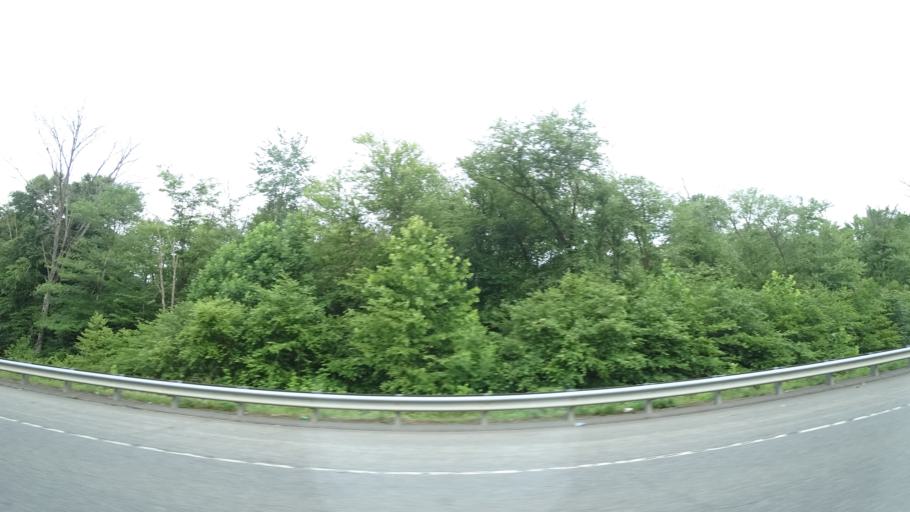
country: US
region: Virginia
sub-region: Spotsylvania County
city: Spotsylvania Courthouse
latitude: 38.1799
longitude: -77.6233
